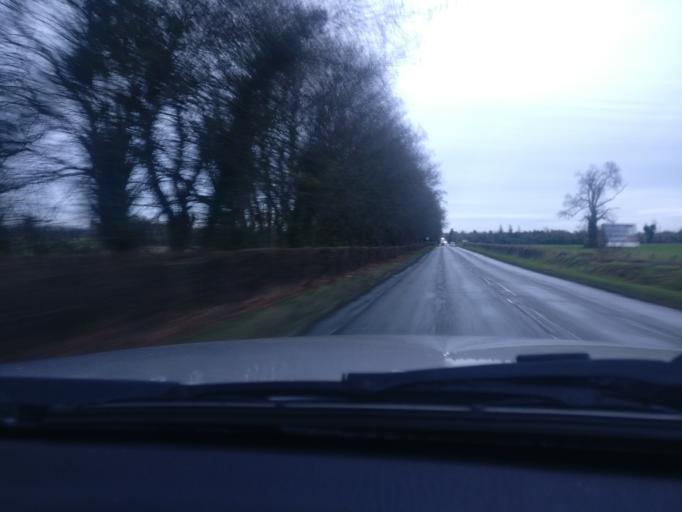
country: IE
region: Leinster
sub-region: An Mhi
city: Navan
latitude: 53.6810
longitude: -6.7574
